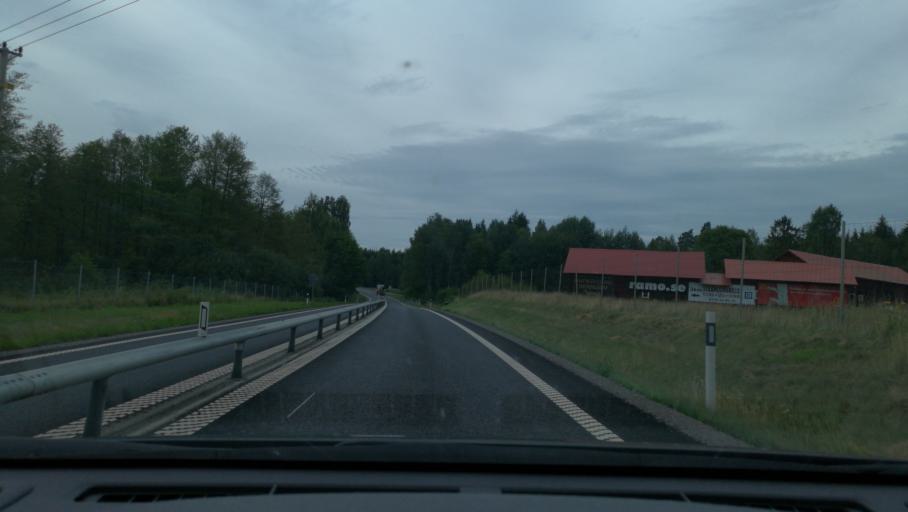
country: SE
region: Soedermanland
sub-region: Katrineholms Kommun
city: Katrineholm
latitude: 58.8552
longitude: 16.2074
